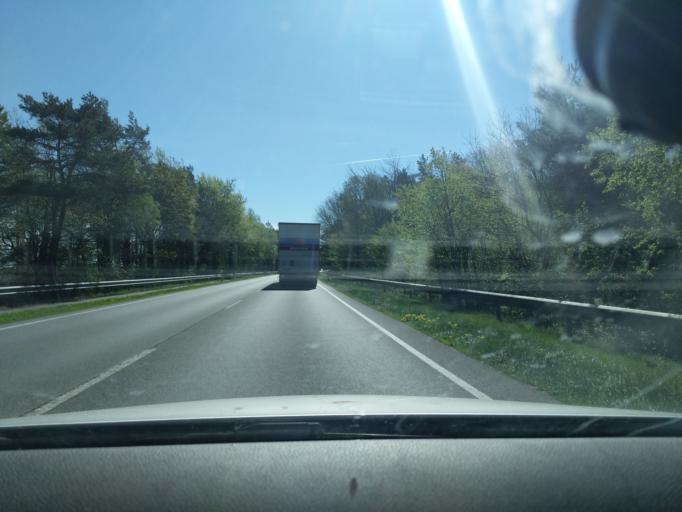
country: DE
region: Lower Saxony
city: Buxtehude
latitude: 53.4596
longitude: 9.7185
